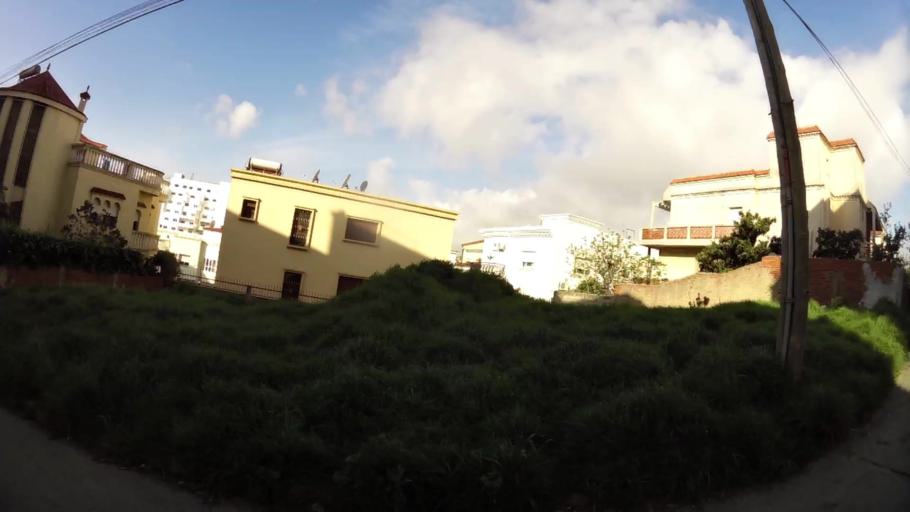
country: MA
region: Tanger-Tetouan
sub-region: Tanger-Assilah
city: Tangier
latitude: 35.7661
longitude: -5.7979
